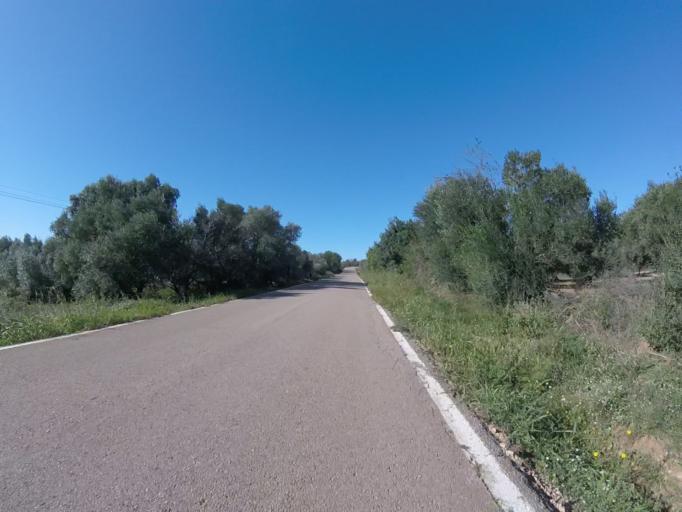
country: ES
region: Valencia
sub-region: Provincia de Castello
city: Chert/Xert
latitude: 40.4517
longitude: 0.1222
